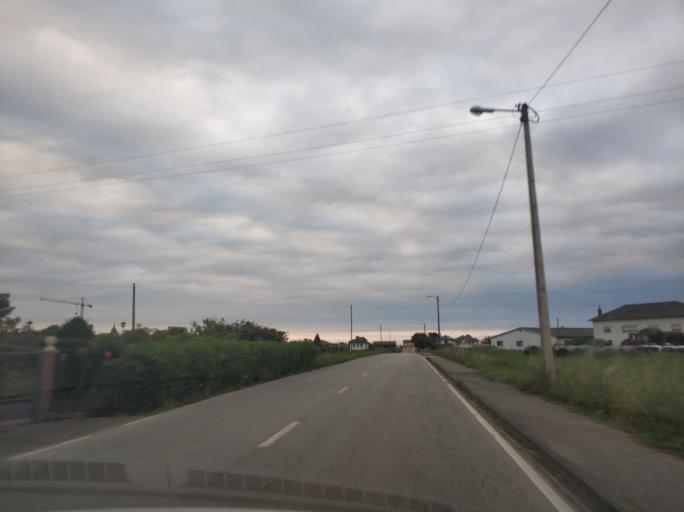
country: ES
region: Asturias
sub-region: Province of Asturias
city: Navia
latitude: 43.5379
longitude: -6.5206
